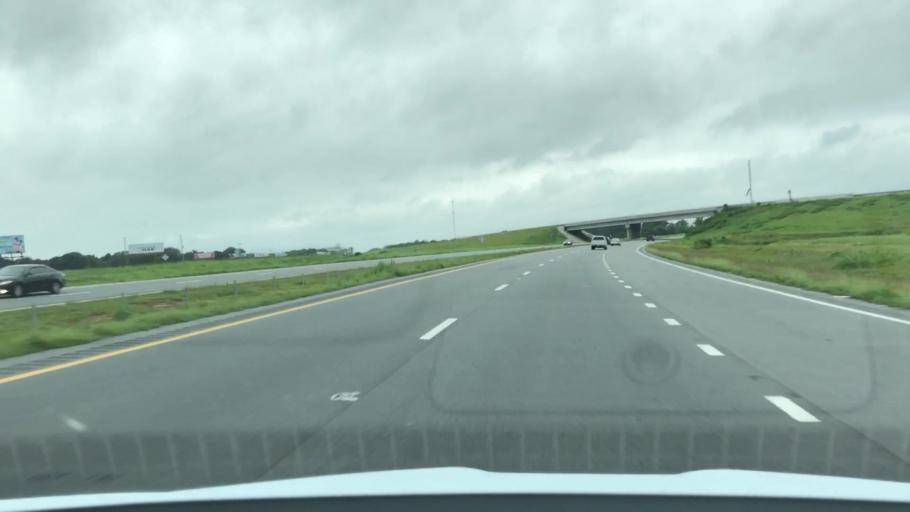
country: US
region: North Carolina
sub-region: Lenoir County
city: La Grange
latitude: 35.3019
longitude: -77.8167
